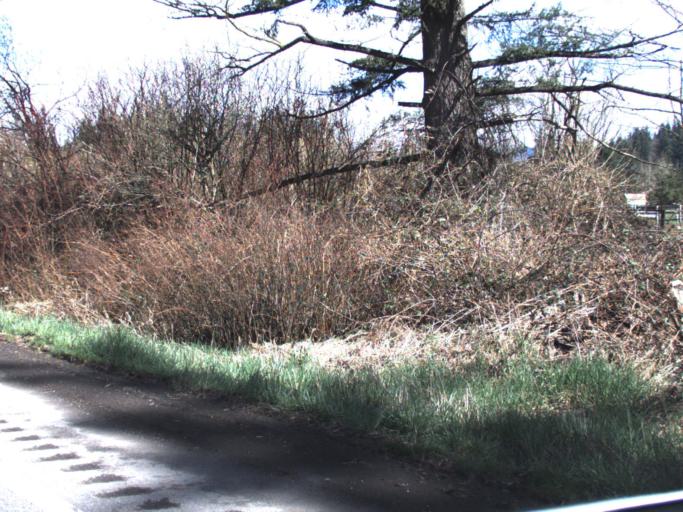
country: US
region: Washington
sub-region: King County
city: Enumclaw
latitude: 47.2383
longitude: -121.9897
